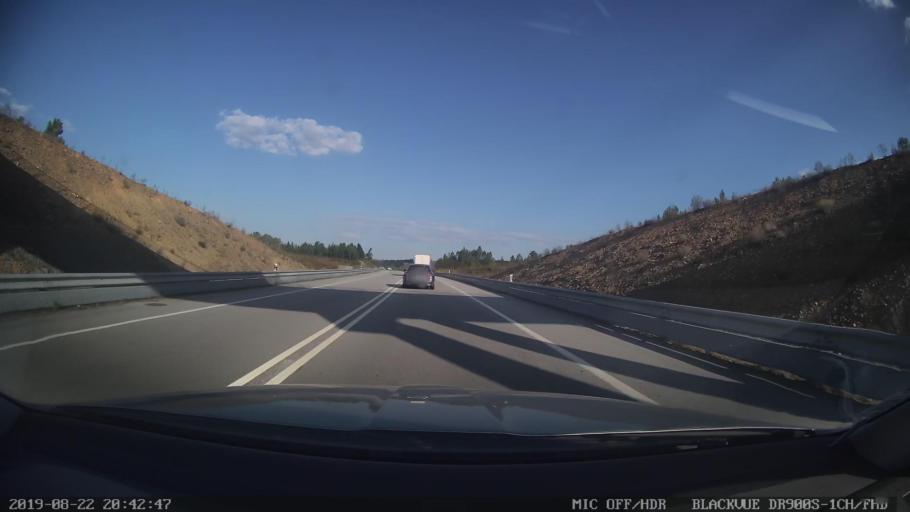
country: PT
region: Castelo Branco
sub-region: Proenca-A-Nova
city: Proenca-a-Nova
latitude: 39.6969
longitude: -7.8213
